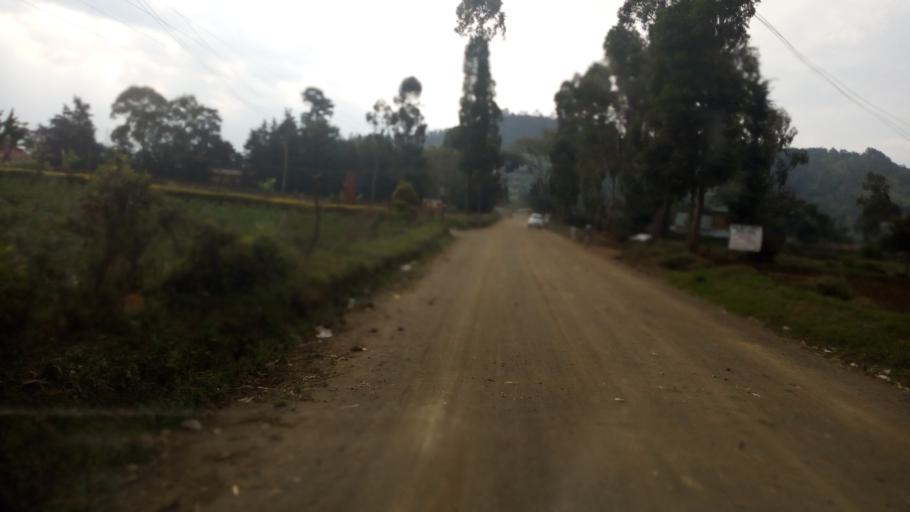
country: UG
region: Western Region
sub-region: Kisoro District
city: Kisoro
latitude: -1.2858
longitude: 29.6895
